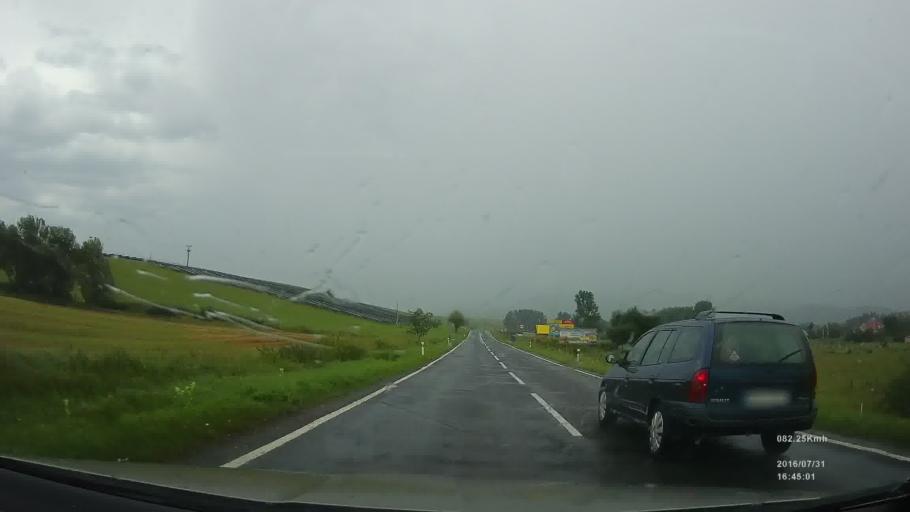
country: SK
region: Presovsky
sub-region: Okres Presov
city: Presov
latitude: 49.0707
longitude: 21.3331
